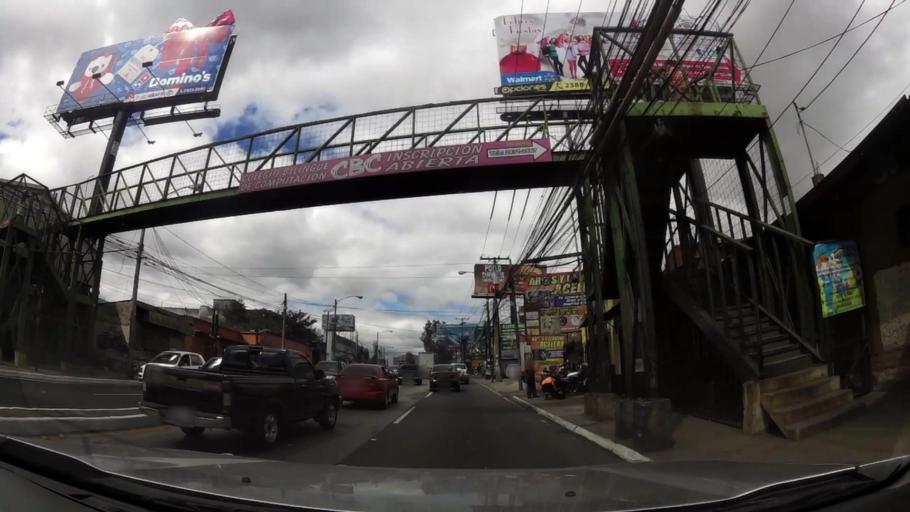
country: GT
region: Guatemala
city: Mixco
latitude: 14.6387
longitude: -90.5643
